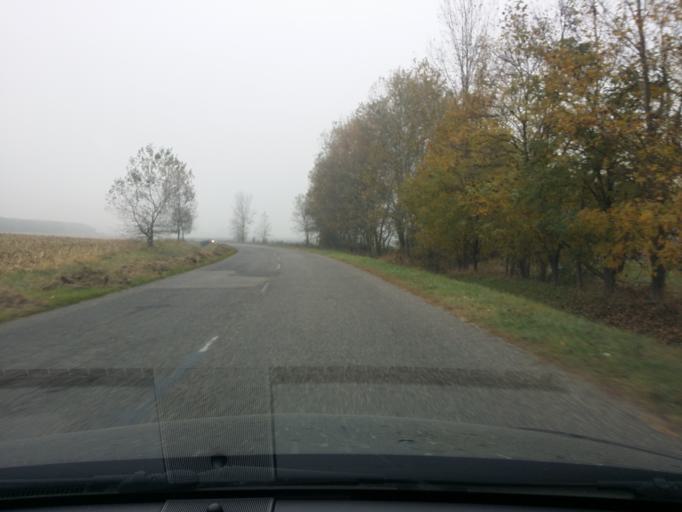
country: HU
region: Szabolcs-Szatmar-Bereg
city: Nyirbogdany
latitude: 48.0468
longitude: 21.8638
